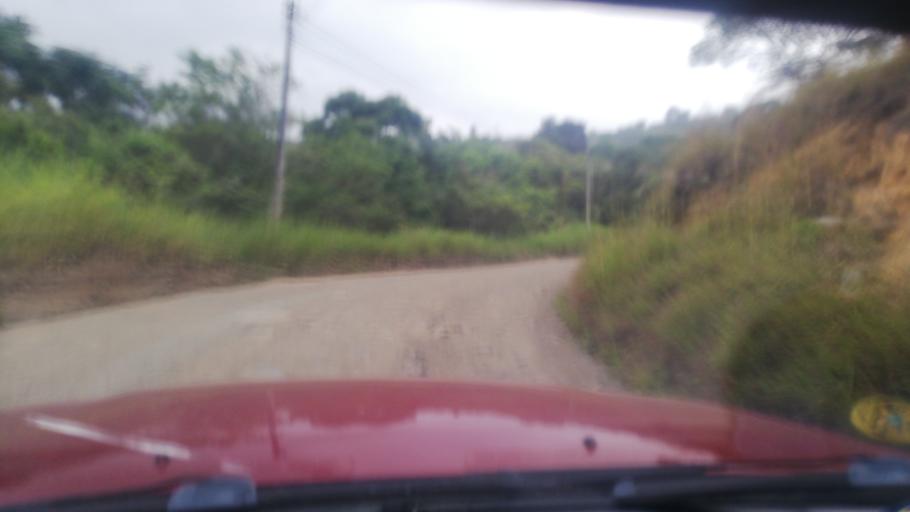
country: CO
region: Valle del Cauca
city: Cali
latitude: 3.4909
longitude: -76.5436
